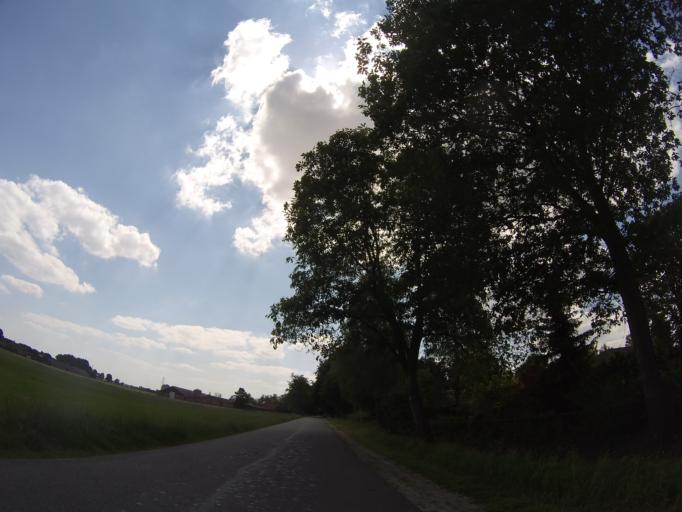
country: NL
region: Gelderland
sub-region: Gemeente Barneveld
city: Stroe
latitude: 52.1918
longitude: 5.6521
